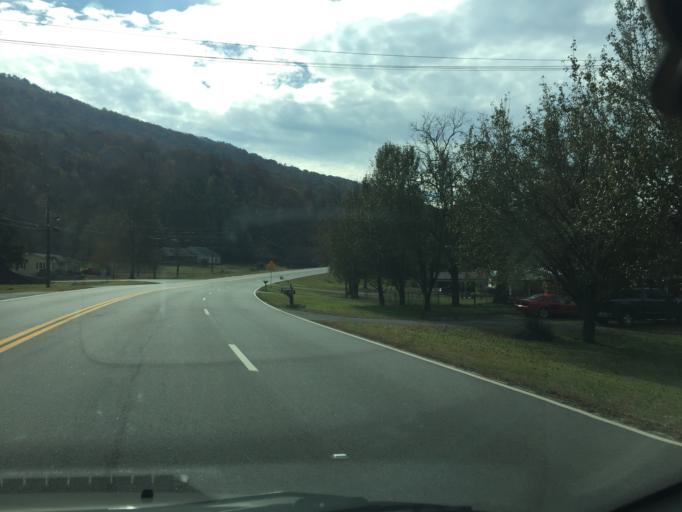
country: US
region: Georgia
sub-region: Dade County
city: Trenton
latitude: 34.8596
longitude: -85.4941
